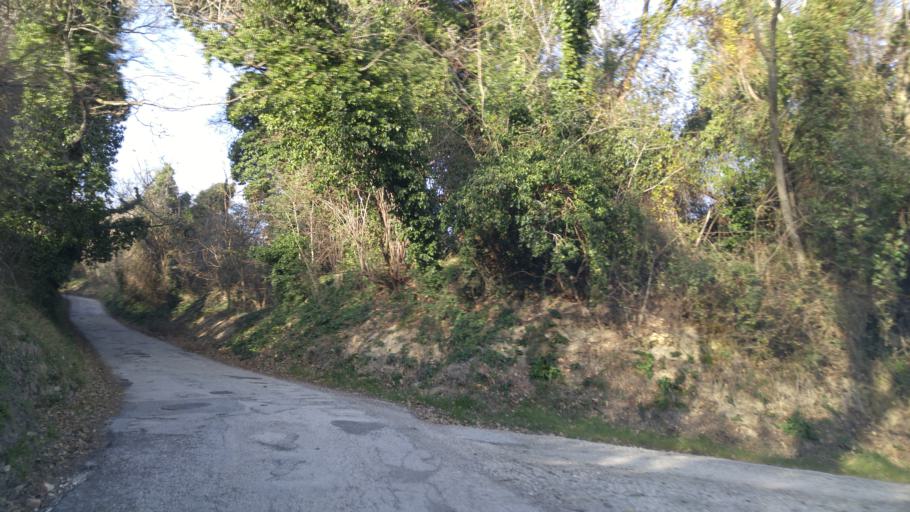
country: IT
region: The Marches
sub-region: Provincia di Pesaro e Urbino
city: Cuccurano
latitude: 43.8220
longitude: 12.9342
